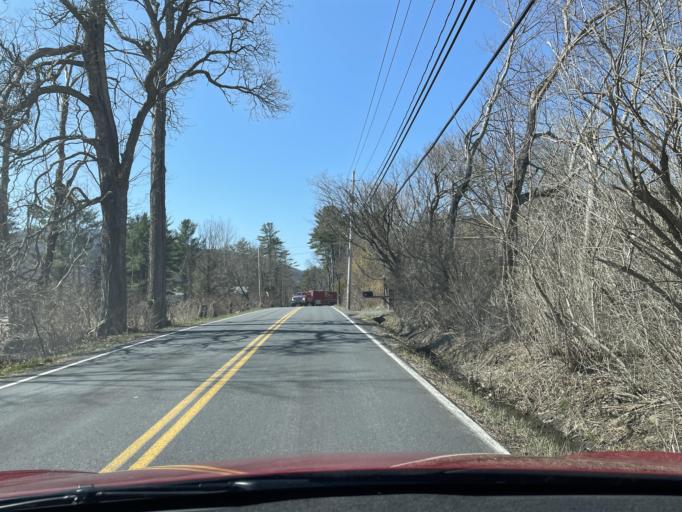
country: US
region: New York
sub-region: Ulster County
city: Shokan
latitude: 42.0275
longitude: -74.1886
